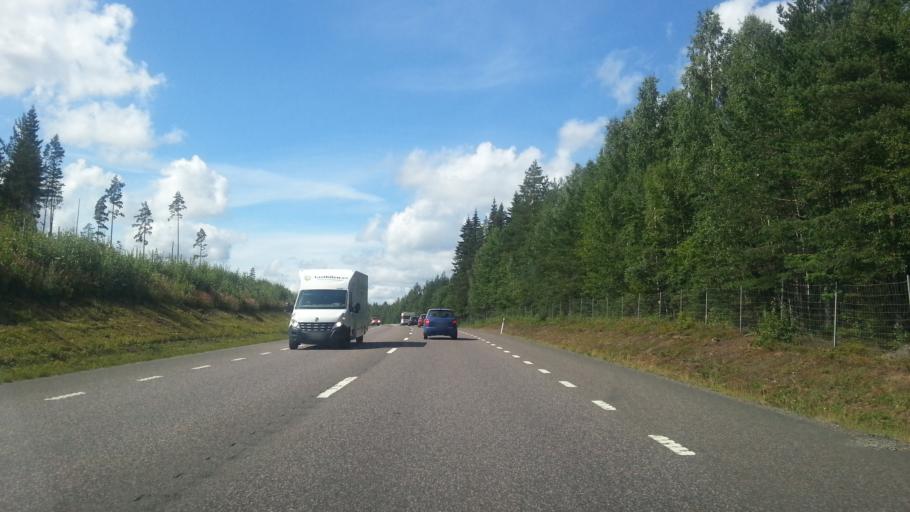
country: SE
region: Dalarna
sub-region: Ludvika Kommun
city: Grangesberg
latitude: 60.0964
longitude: 15.0727
